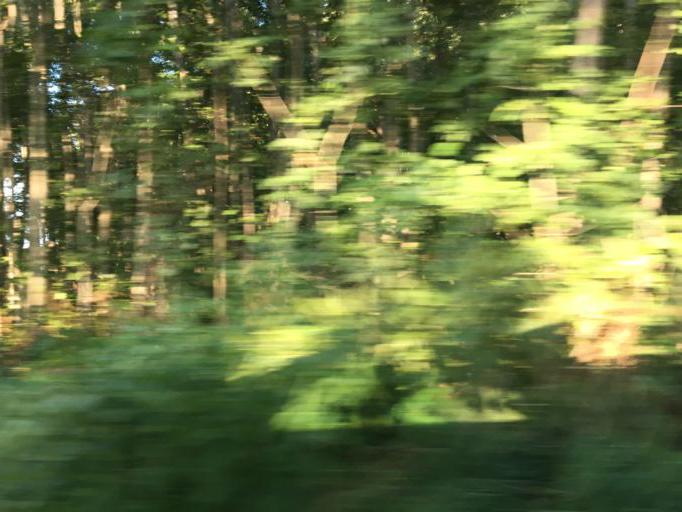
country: DE
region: Saxony
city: Wilsdruff
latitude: 51.0675
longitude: 13.5874
